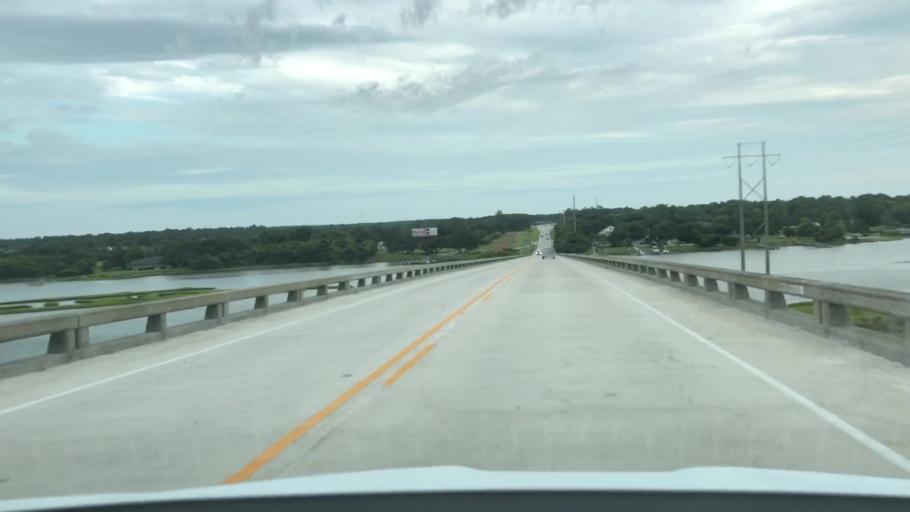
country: US
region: North Carolina
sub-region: Carteret County
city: Cedar Point
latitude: 34.6754
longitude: -77.0658
